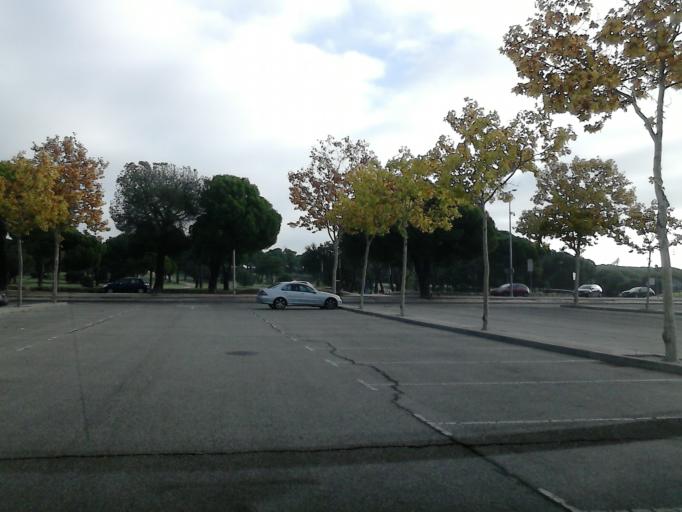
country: ES
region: Madrid
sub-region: Provincia de Madrid
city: Las Rozas de Madrid
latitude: 40.5108
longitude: -3.8930
